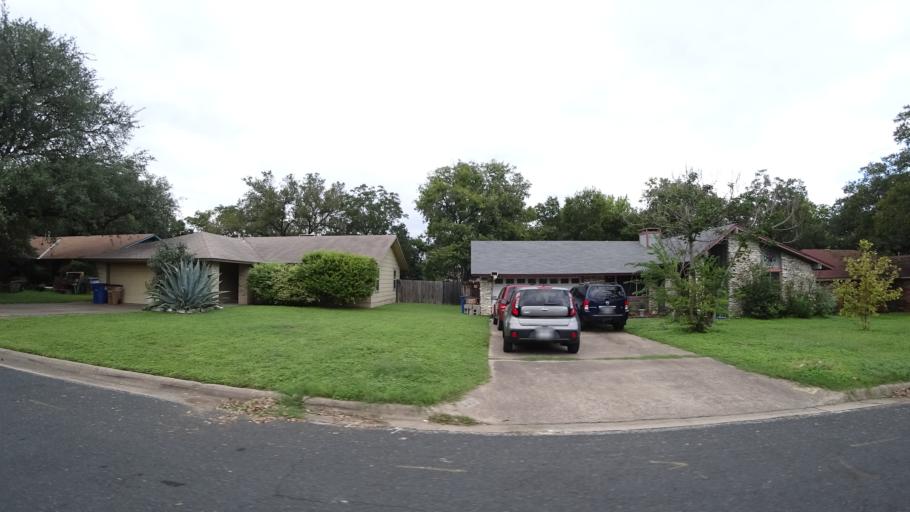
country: US
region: Texas
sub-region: Travis County
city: Rollingwood
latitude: 30.2111
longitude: -97.7848
